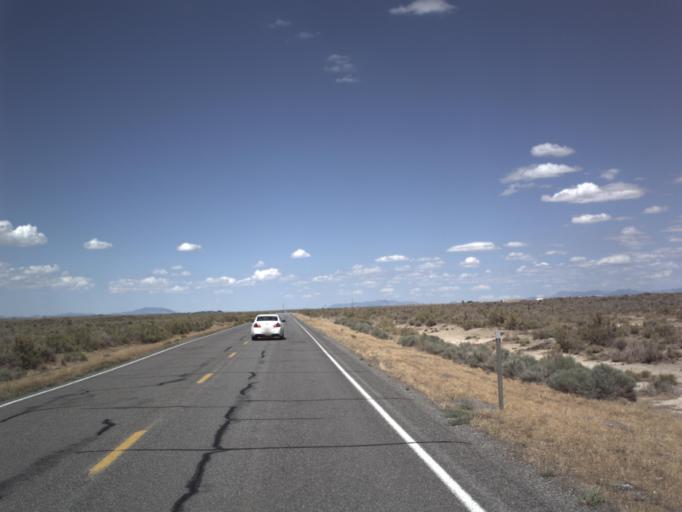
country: US
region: Utah
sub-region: Millard County
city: Delta
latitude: 39.3007
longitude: -112.4717
